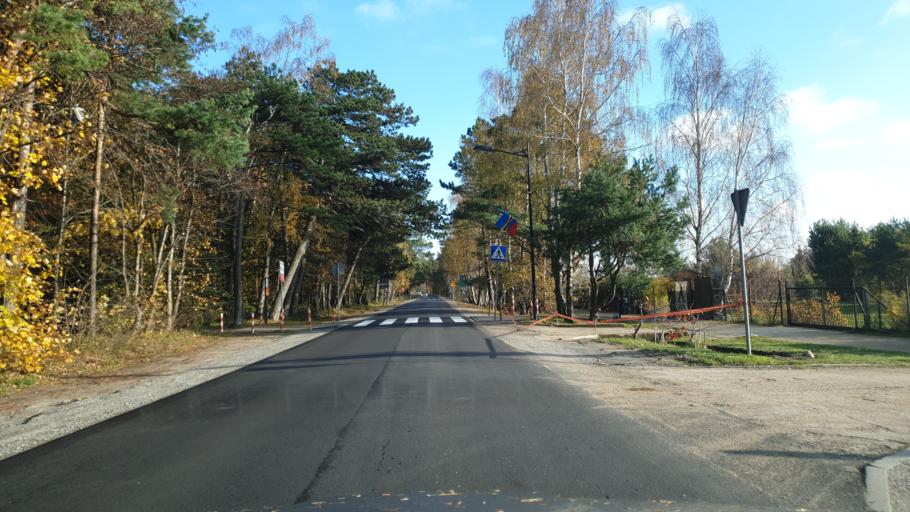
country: PL
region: Pomeranian Voivodeship
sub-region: Powiat pucki
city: Krokowa
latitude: 54.8306
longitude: 18.2254
